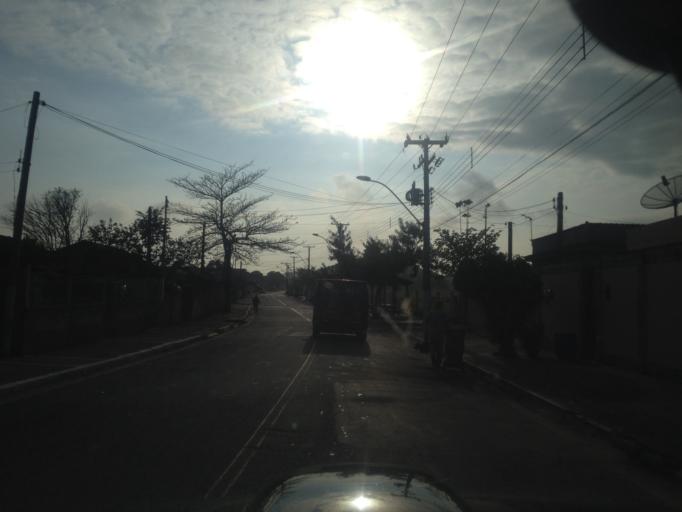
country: BR
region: Rio de Janeiro
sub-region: Porto Real
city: Porto Real
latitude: -22.4614
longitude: -44.3447
